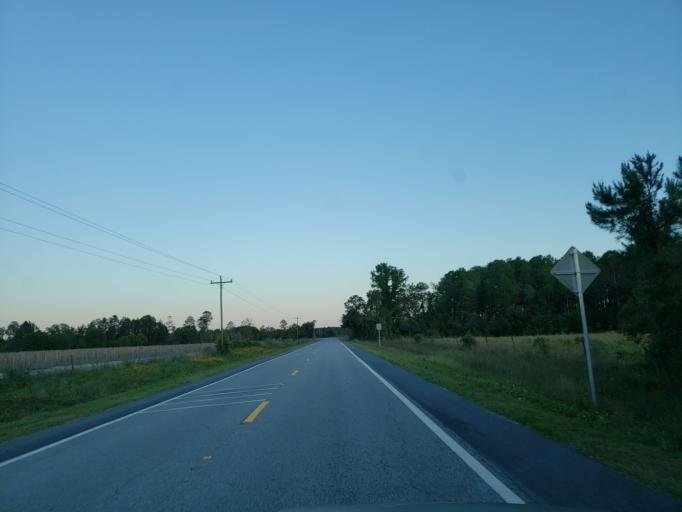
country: US
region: Georgia
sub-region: Echols County
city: Statenville
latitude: 30.5681
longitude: -83.1581
